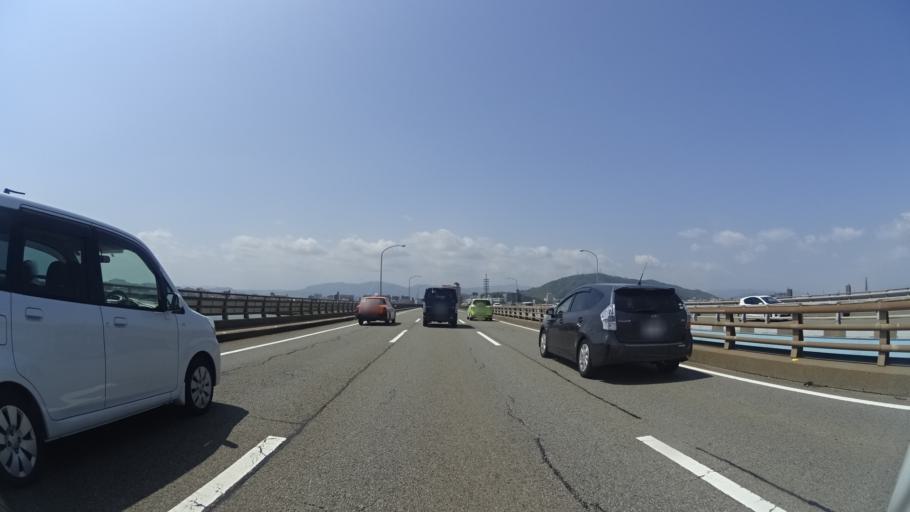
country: JP
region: Tokushima
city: Tokushima-shi
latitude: 34.0897
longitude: 134.5682
